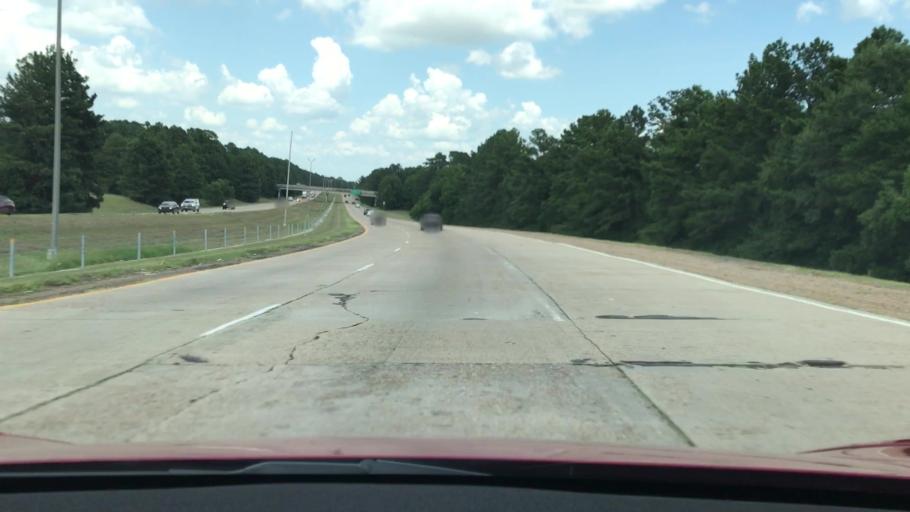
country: US
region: Louisiana
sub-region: Bossier Parish
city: Bossier City
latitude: 32.4156
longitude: -93.7848
